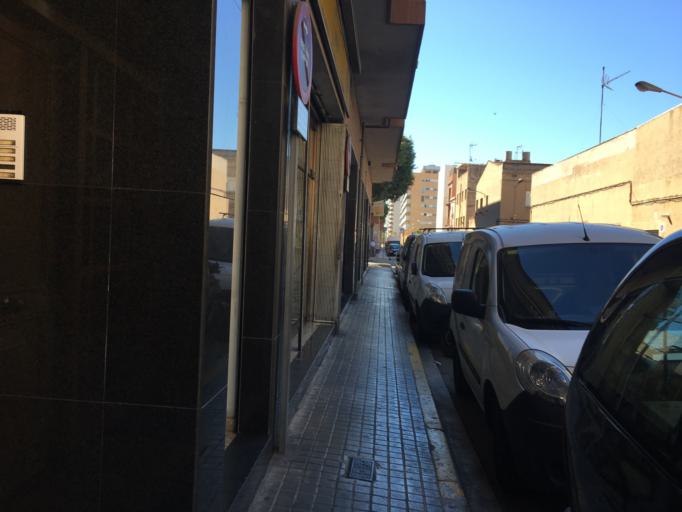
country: ES
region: Catalonia
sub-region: Provincia de Barcelona
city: Badalona
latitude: 41.4416
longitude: 2.2401
